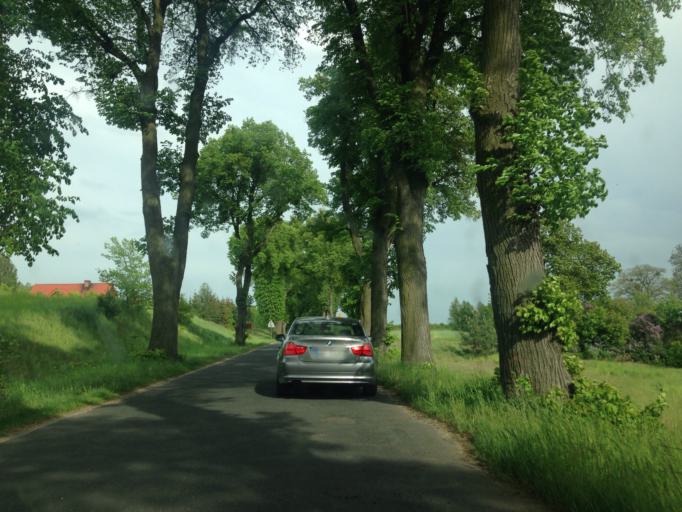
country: PL
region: Kujawsko-Pomorskie
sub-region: Powiat brodnicki
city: Brodnica
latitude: 53.2798
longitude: 19.4364
